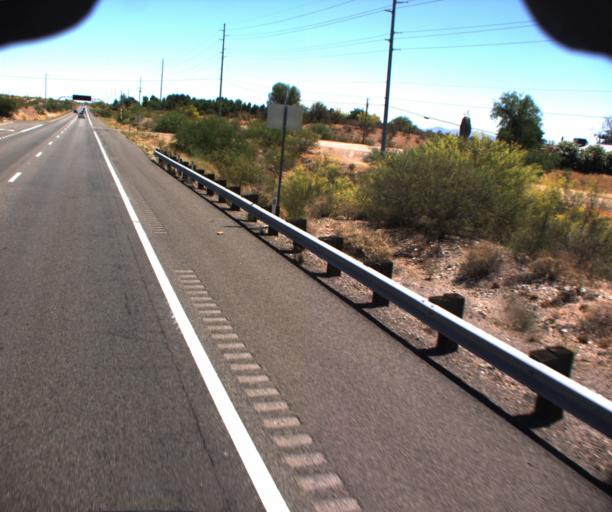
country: US
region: Arizona
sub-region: Maricopa County
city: Wickenburg
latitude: 33.8742
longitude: -112.6463
